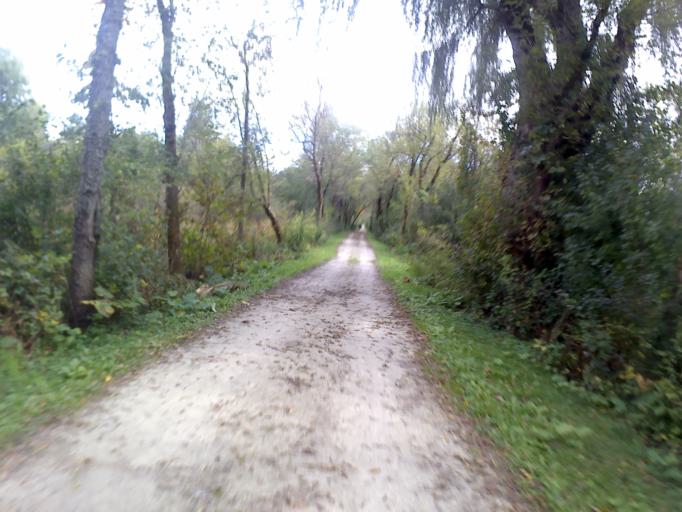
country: US
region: Illinois
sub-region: DuPage County
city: Winfield
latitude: 41.8928
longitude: -88.1605
